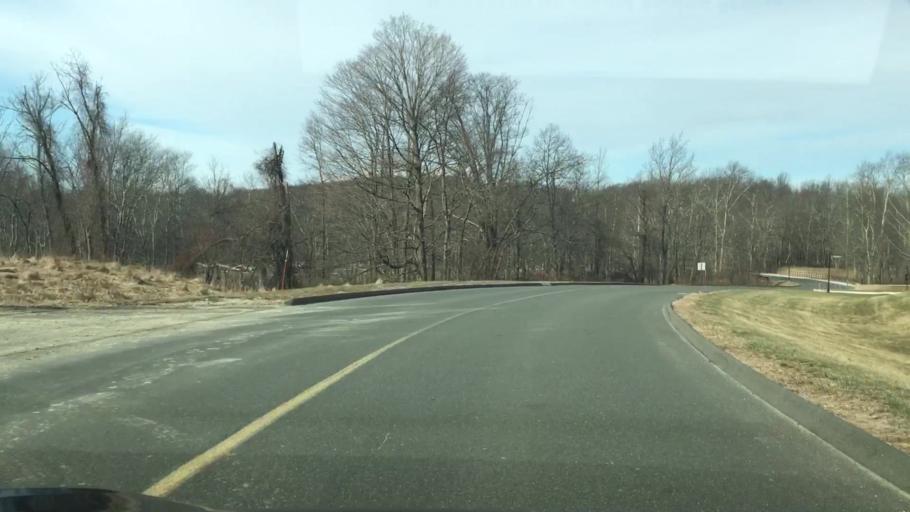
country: US
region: New York
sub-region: Putnam County
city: Peach Lake
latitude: 41.3729
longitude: -73.5144
